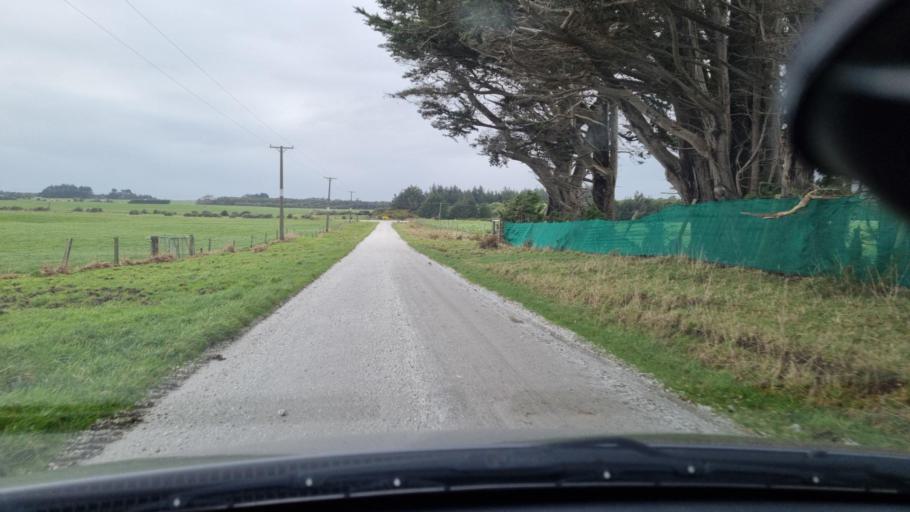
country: NZ
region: Southland
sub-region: Invercargill City
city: Invercargill
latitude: -46.4461
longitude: 168.4206
